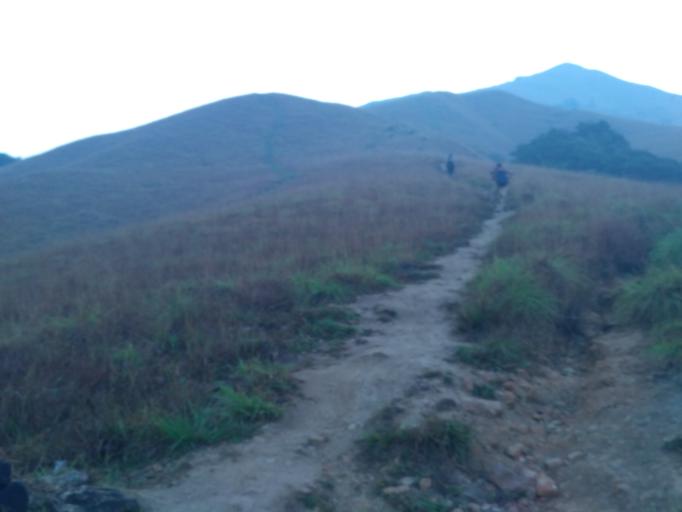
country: IN
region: Karnataka
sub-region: Kodagu
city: Somvarpet
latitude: 12.6641
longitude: 75.6627
